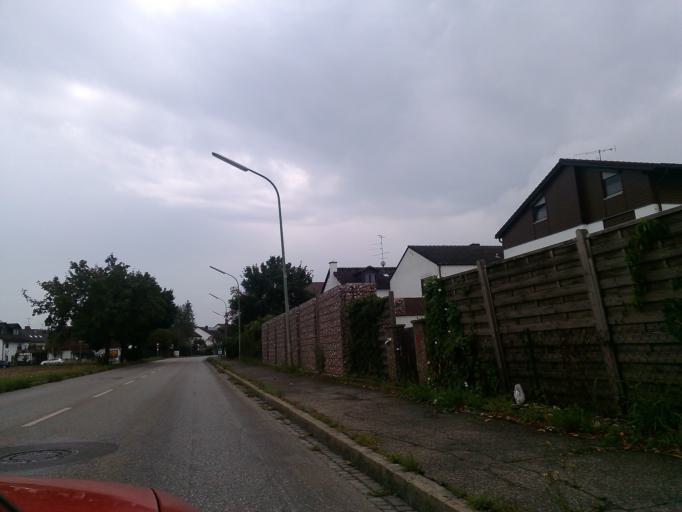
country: DE
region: Bavaria
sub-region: Upper Bavaria
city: Olching
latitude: 48.1943
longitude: 11.3258
